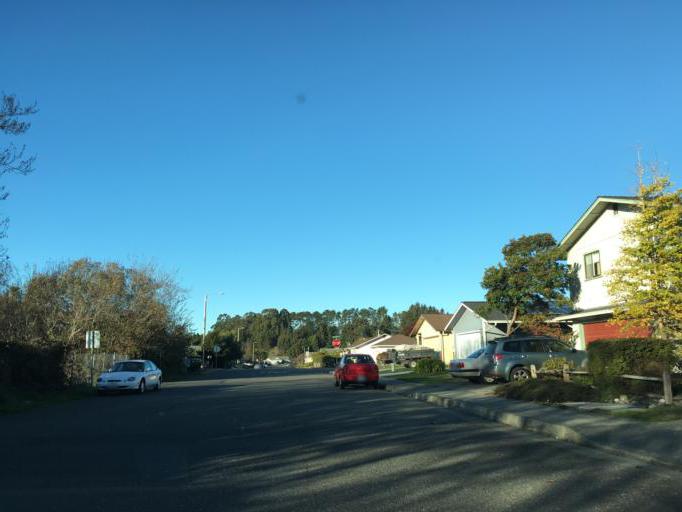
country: US
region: California
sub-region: Humboldt County
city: McKinleyville
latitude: 40.9604
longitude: -124.1051
